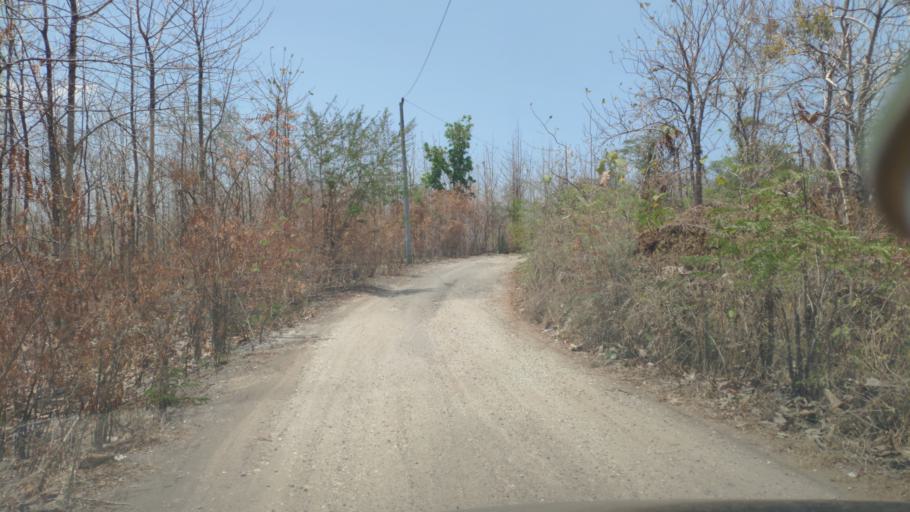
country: ID
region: Central Java
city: Randublatung
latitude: -7.2705
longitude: 111.3786
